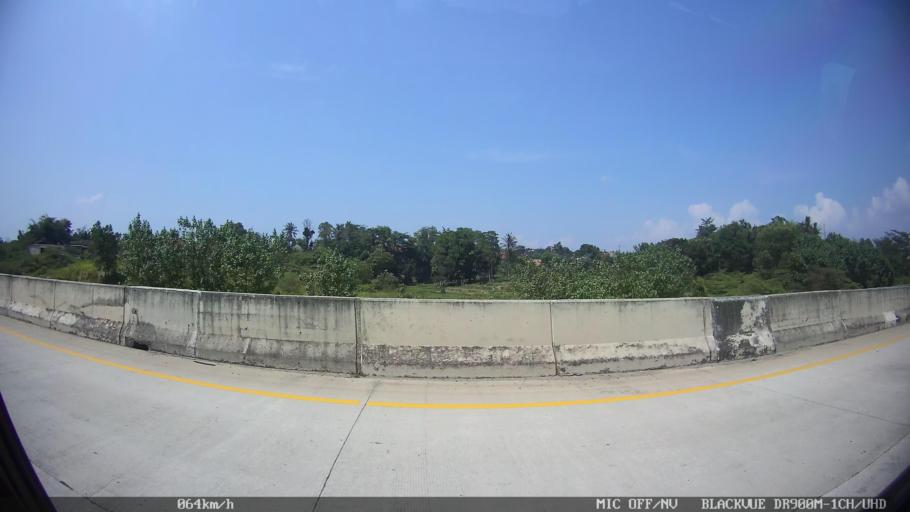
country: ID
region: Lampung
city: Kedaton
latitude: -5.3348
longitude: 105.2992
